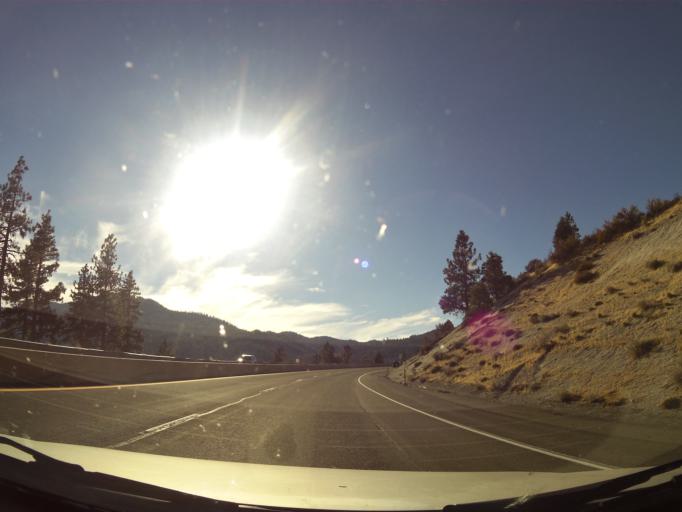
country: US
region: Nevada
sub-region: Douglas County
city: Indian Hills
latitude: 39.1169
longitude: -119.8486
